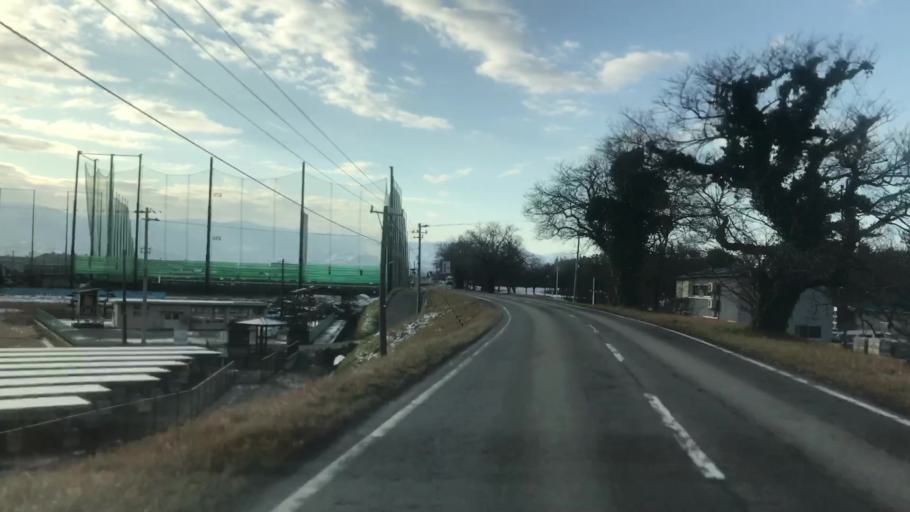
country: JP
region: Toyama
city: Toyama-shi
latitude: 36.6976
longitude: 137.2823
